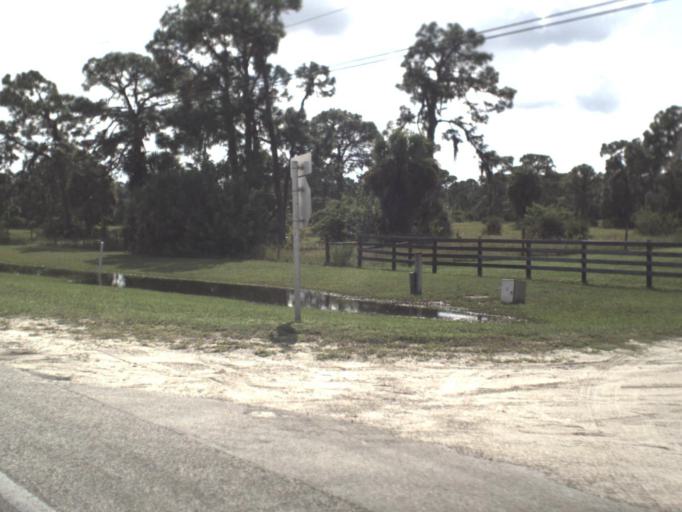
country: US
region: Florida
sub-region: Sarasota County
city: Plantation
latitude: 27.0495
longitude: -82.3360
